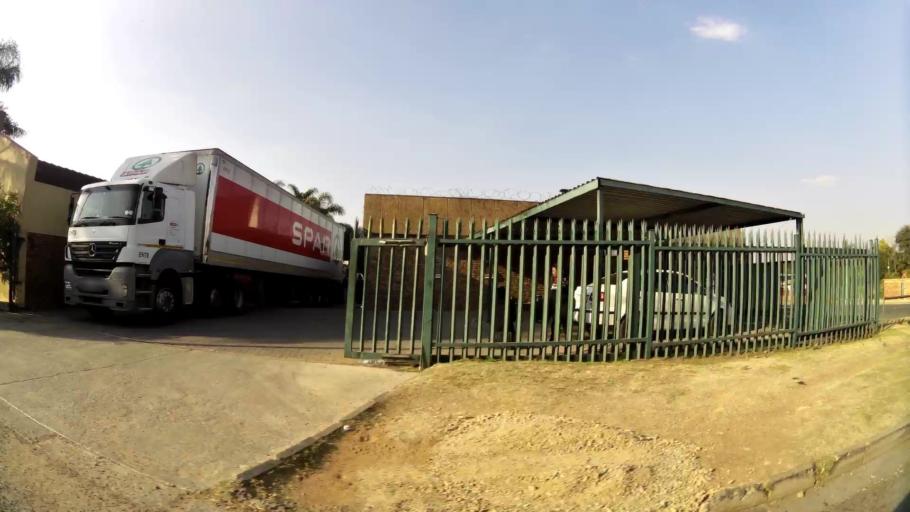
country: ZA
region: Gauteng
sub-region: City of Johannesburg Metropolitan Municipality
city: Modderfontein
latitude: -26.0813
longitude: 28.2097
